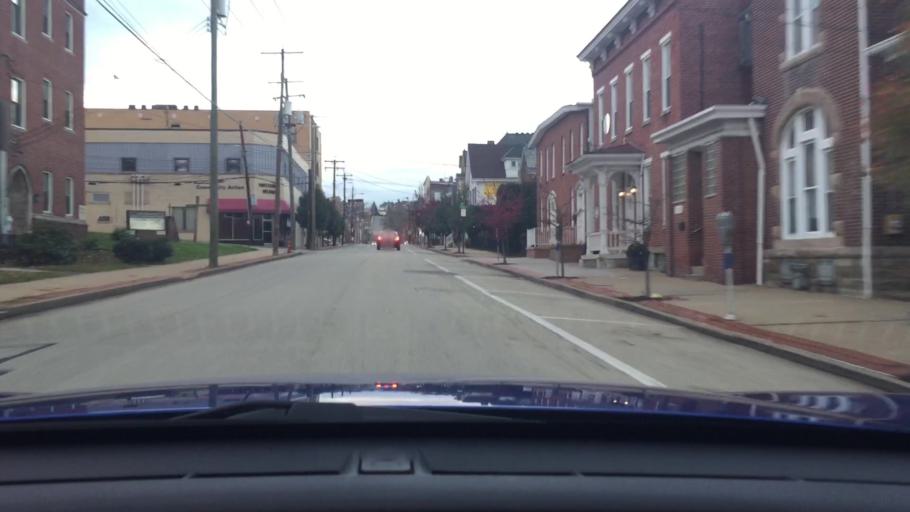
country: US
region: Pennsylvania
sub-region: Westmoreland County
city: Greensburg
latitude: 40.2999
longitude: -79.5423
